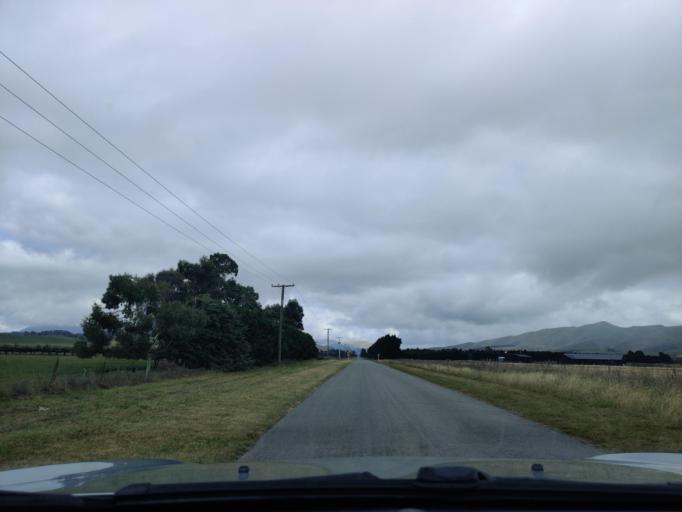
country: NZ
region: Canterbury
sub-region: Hurunui District
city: Amberley
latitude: -43.0755
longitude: 172.6934
